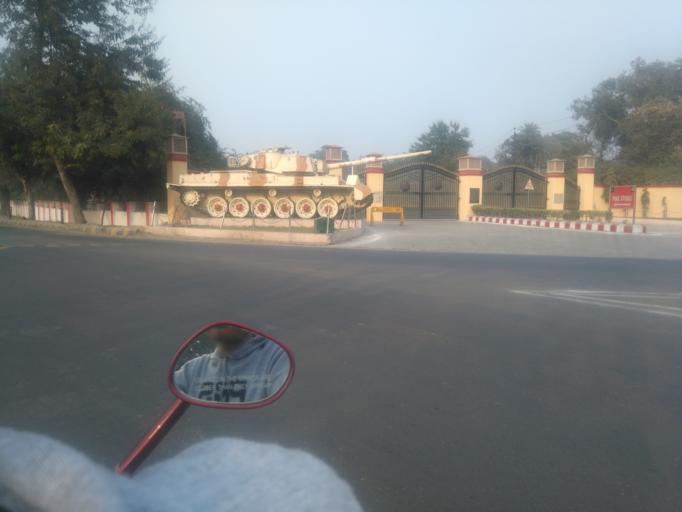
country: IN
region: Uttar Pradesh
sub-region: Meerut
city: Meerut
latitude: 29.0082
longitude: 77.6914
